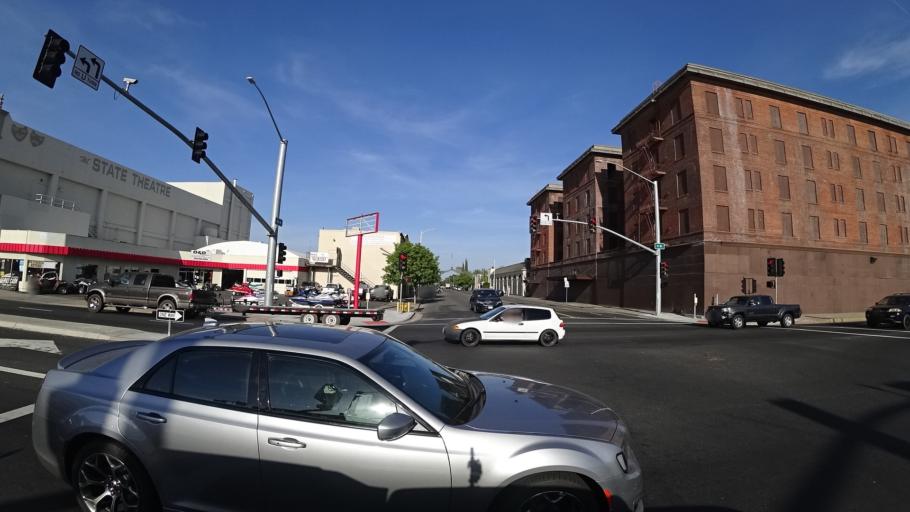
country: US
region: California
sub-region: Yuba County
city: Marysville
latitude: 39.1403
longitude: -121.5907
